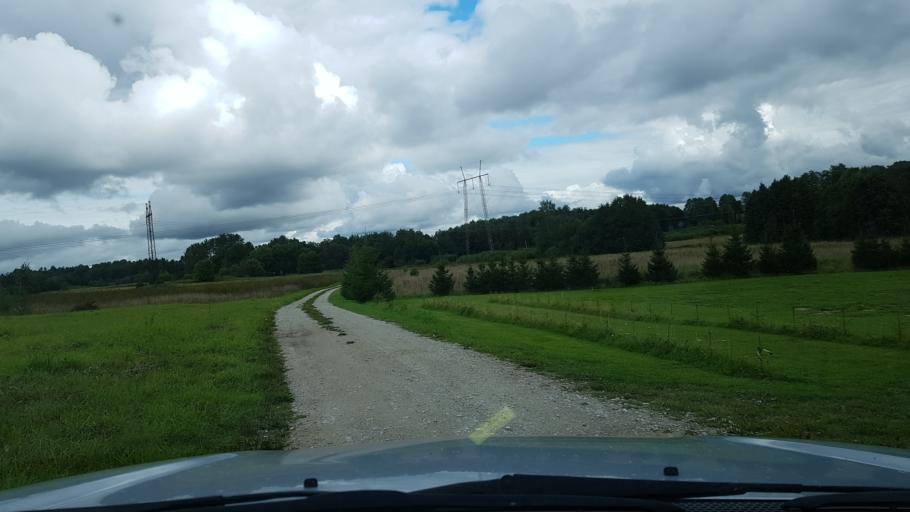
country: EE
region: Harju
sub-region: Raasiku vald
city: Arukula
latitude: 59.2704
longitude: 25.1042
